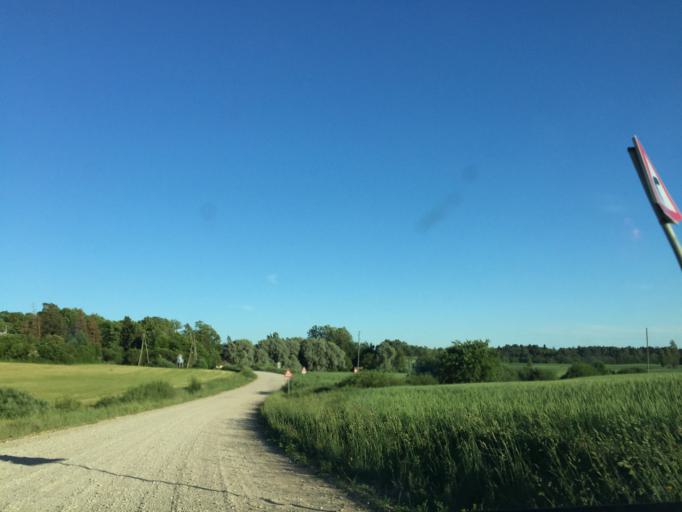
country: LV
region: Broceni
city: Broceni
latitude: 56.7871
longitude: 22.5608
